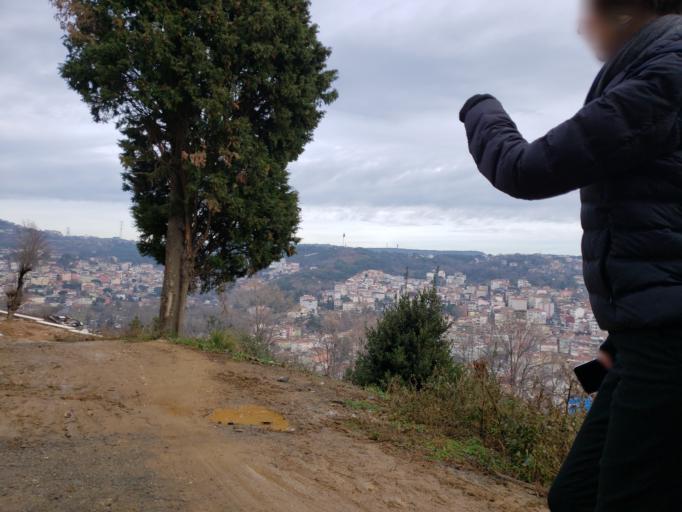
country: TR
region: Istanbul
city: Arikoey
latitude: 41.1674
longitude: 29.0540
